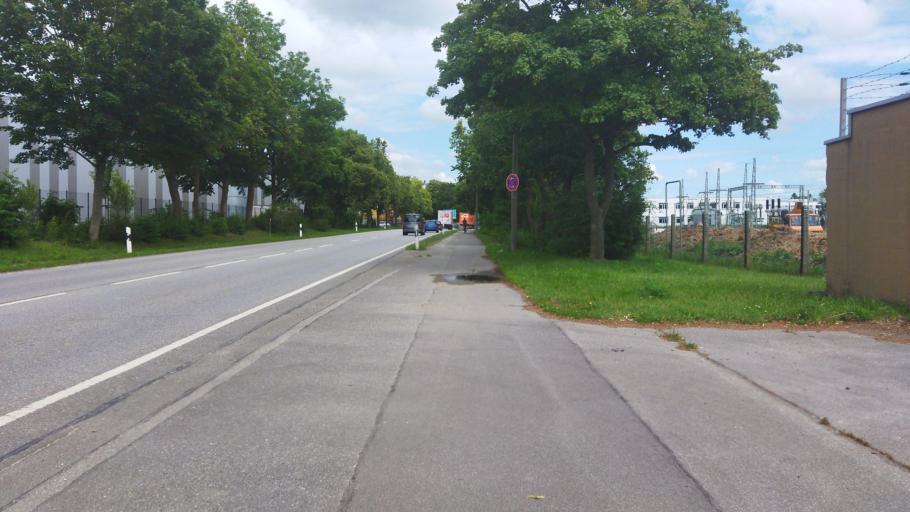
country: DE
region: Bavaria
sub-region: Upper Palatinate
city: Tegernheim
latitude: 49.0136
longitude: 12.1508
